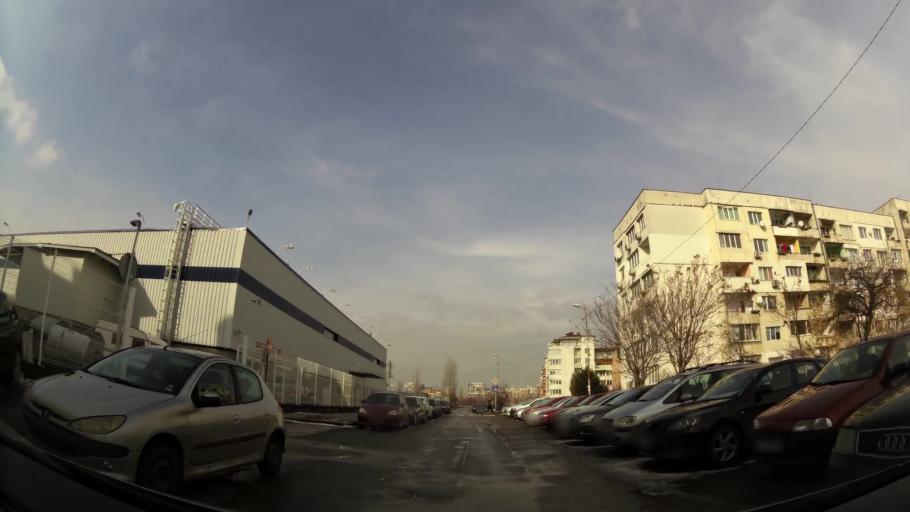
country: BG
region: Sofiya
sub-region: Obshtina Bozhurishte
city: Bozhurishte
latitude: 42.7196
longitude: 23.2582
